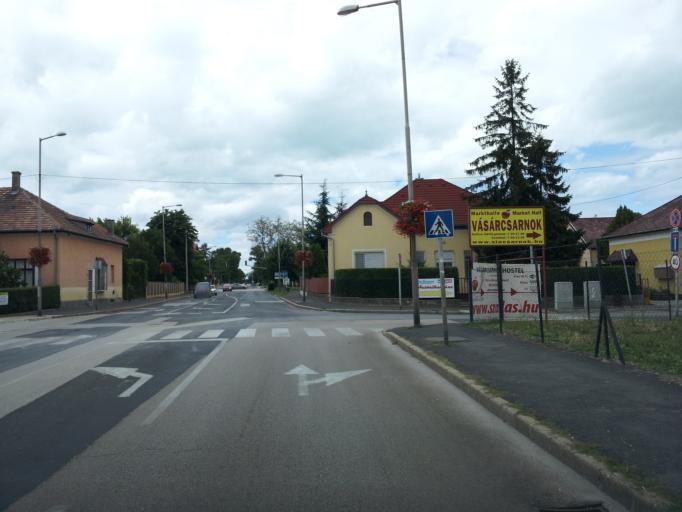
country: HU
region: Somogy
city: Siofok
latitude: 46.9033
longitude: 18.0470
